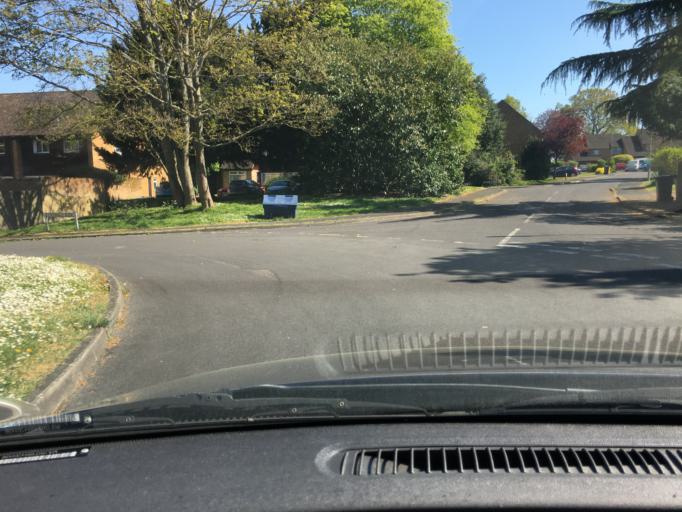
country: GB
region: England
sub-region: Hampshire
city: Yateley
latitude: 51.3362
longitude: -0.8177
